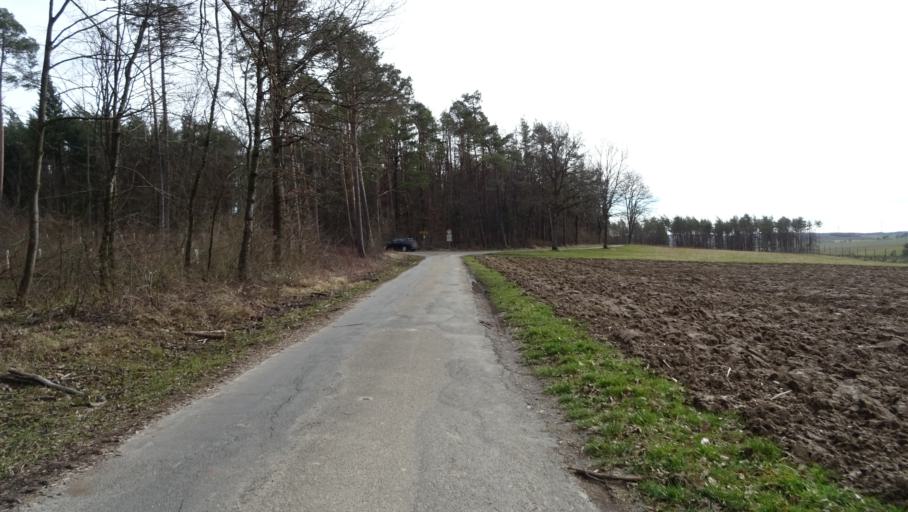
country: DE
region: Baden-Wuerttemberg
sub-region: Karlsruhe Region
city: Limbach
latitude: 49.4371
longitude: 9.2668
